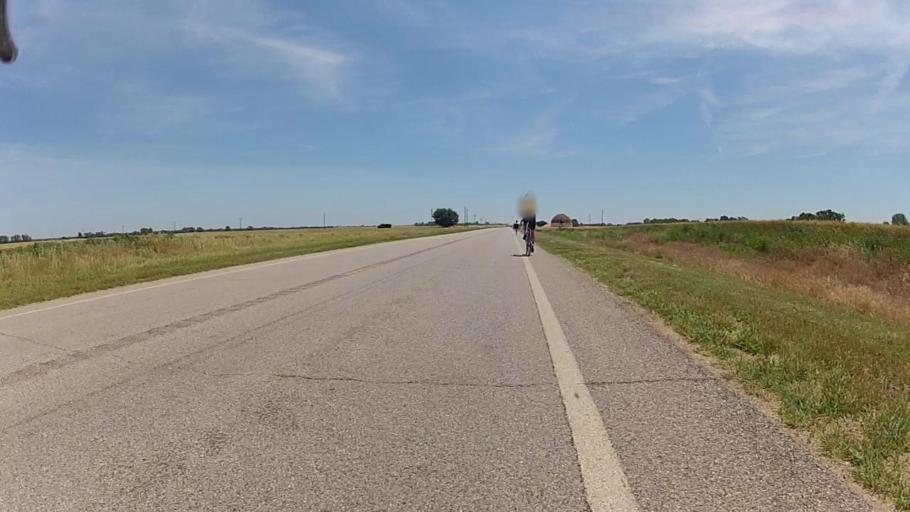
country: US
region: Kansas
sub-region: Barber County
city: Medicine Lodge
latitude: 37.2543
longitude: -98.5162
